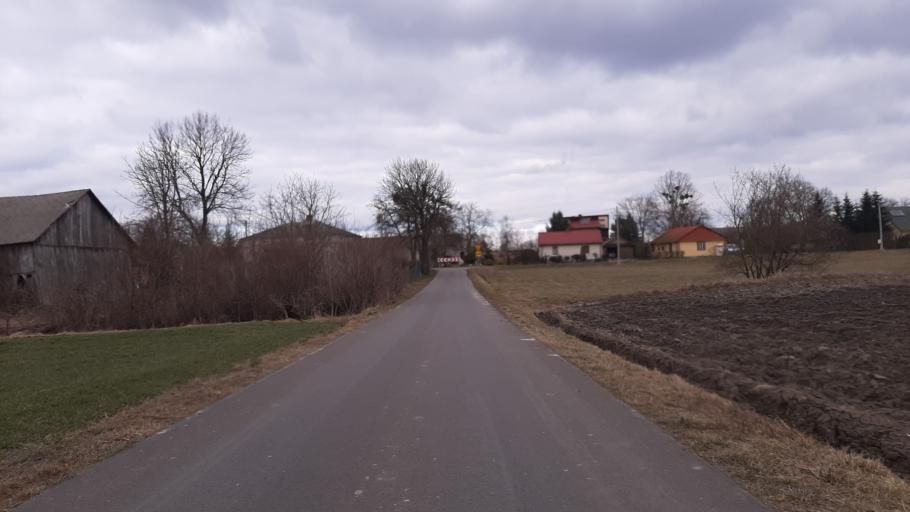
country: PL
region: Lublin Voivodeship
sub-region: Powiat lubelski
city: Garbow
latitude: 51.3520
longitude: 22.3931
